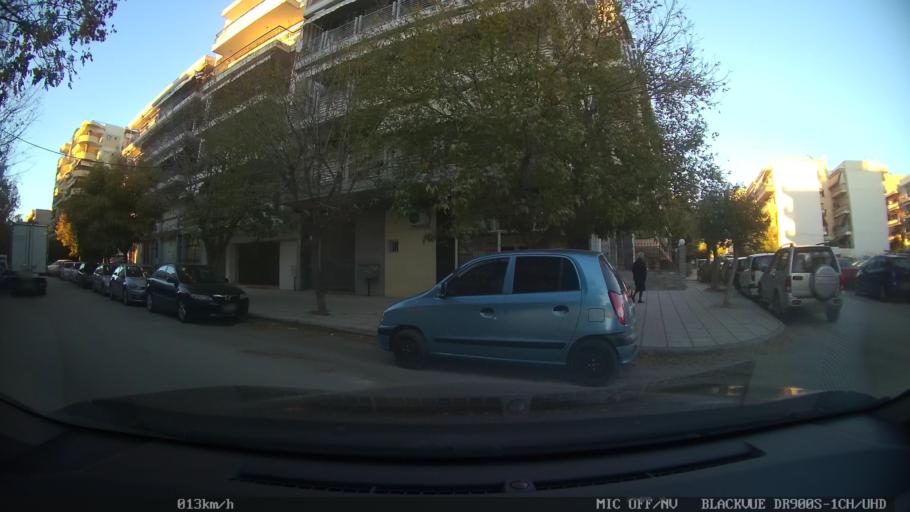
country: GR
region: Central Macedonia
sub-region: Nomos Thessalonikis
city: Pylaia
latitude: 40.6055
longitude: 22.9805
